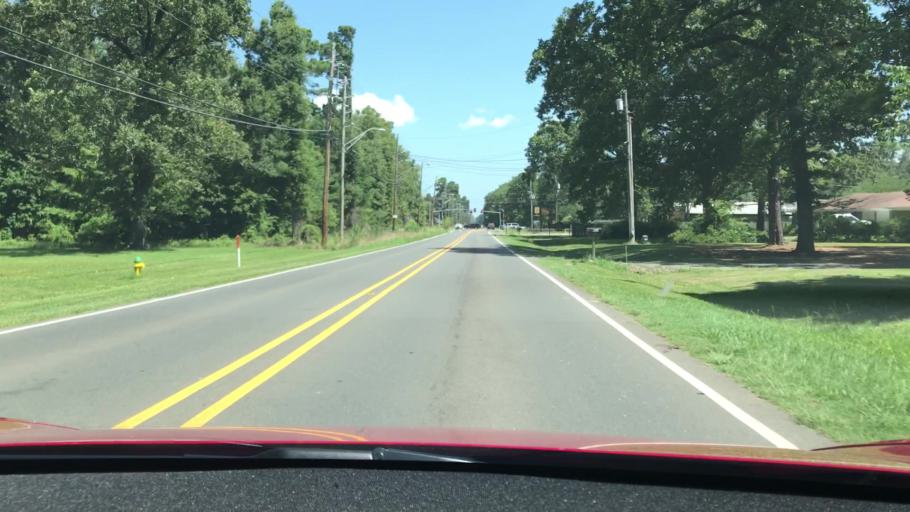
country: US
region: Louisiana
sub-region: De Soto Parish
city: Stonewall
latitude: 32.3525
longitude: -93.7138
